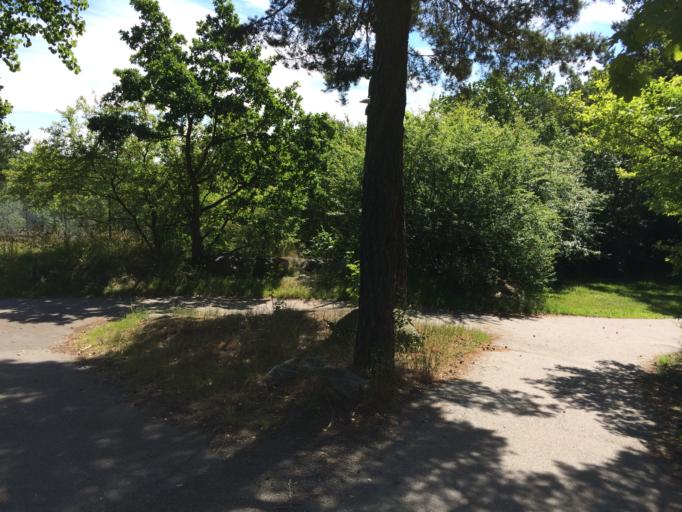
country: SE
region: Stockholm
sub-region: Huddinge Kommun
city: Segeltorp
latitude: 59.2971
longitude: 17.9865
